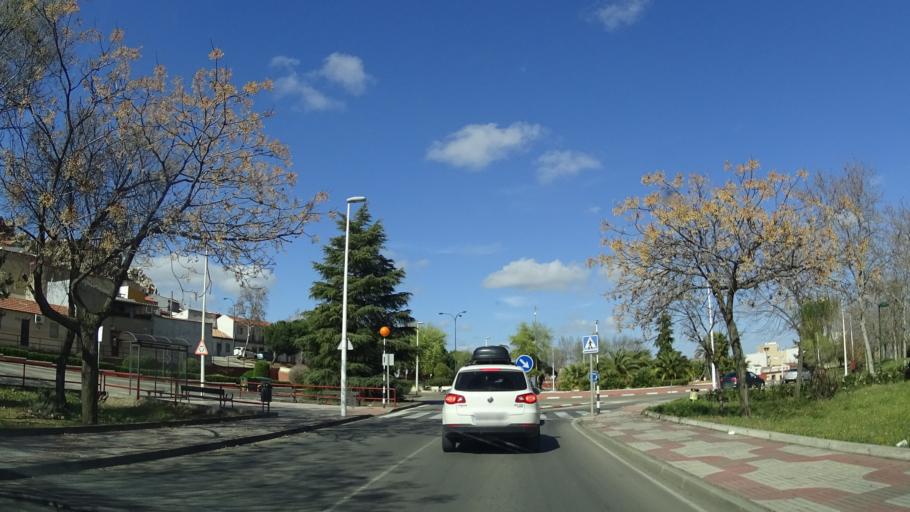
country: ES
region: Castille-La Mancha
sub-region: Provincia de Ciudad Real
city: Puertollano
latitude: 38.6932
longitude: -4.1125
